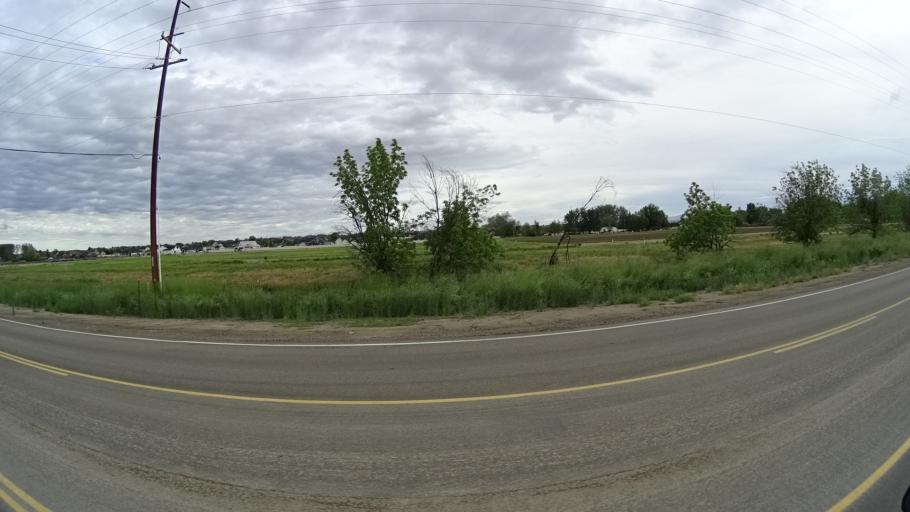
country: US
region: Idaho
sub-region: Ada County
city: Star
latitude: 43.6921
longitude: -116.5015
